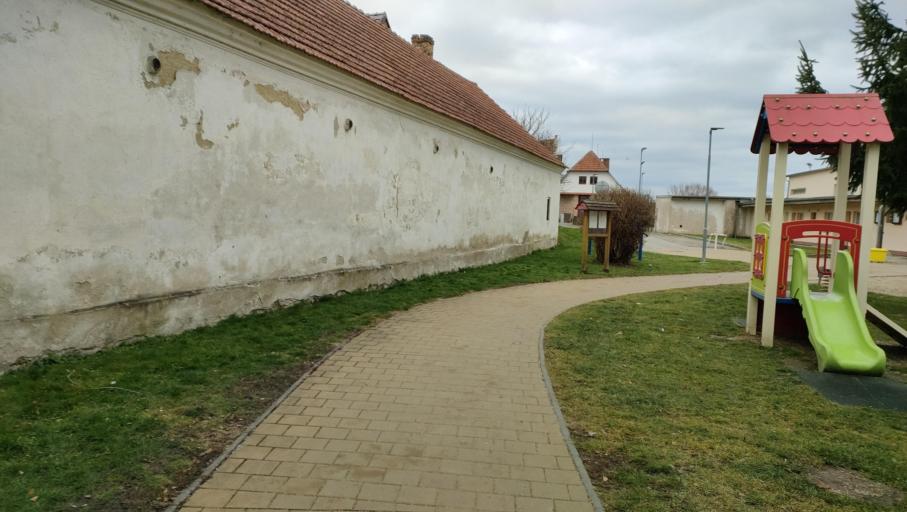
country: CZ
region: South Moravian
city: Sokolnice
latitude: 49.1376
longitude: 16.7316
